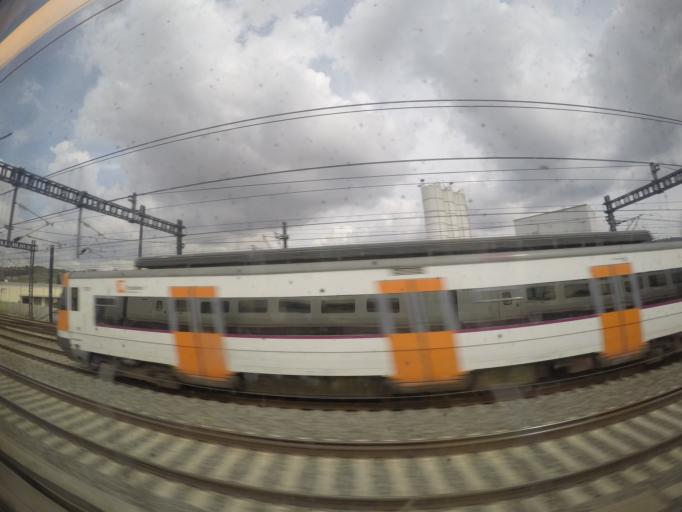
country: ES
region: Catalonia
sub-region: Provincia de Barcelona
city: Sant Andreu de la Barca
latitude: 41.4481
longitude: 1.9876
